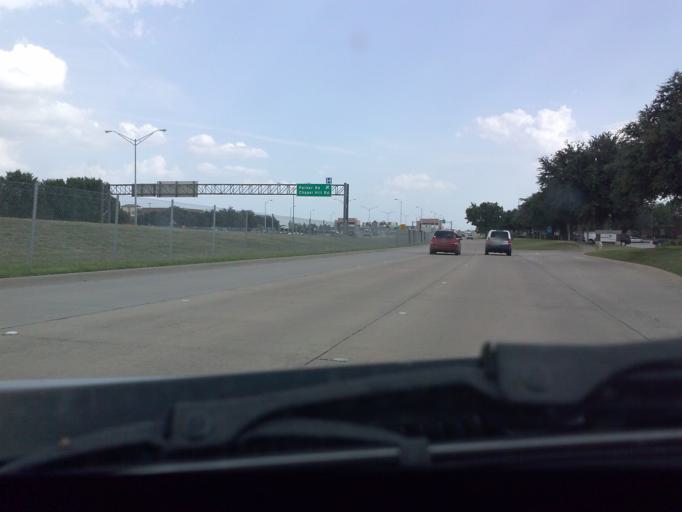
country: US
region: Texas
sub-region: Denton County
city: The Colony
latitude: 33.0517
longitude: -96.8303
